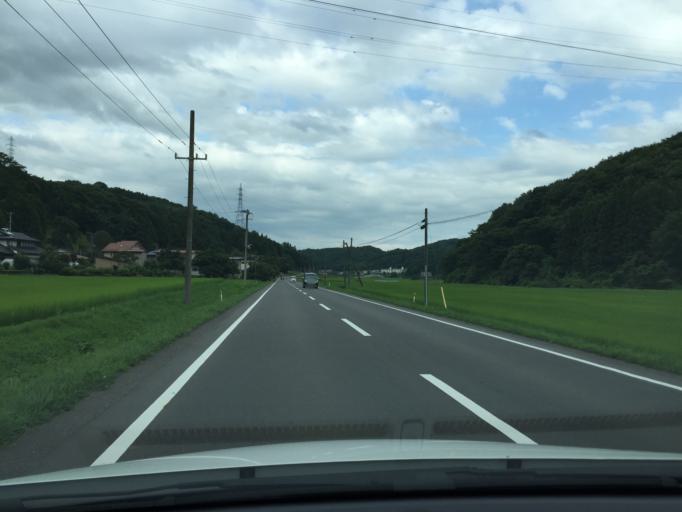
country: JP
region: Fukushima
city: Sukagawa
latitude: 37.1849
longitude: 140.2038
